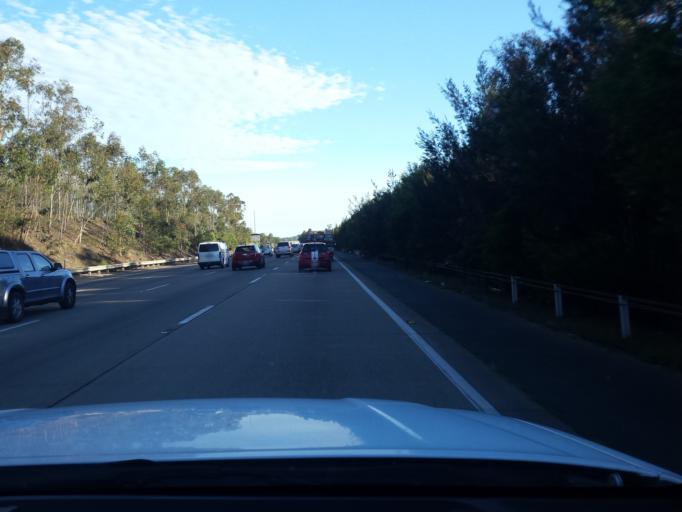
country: AU
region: Queensland
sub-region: Gold Coast
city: Oxenford
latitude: -27.8402
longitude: 153.3037
